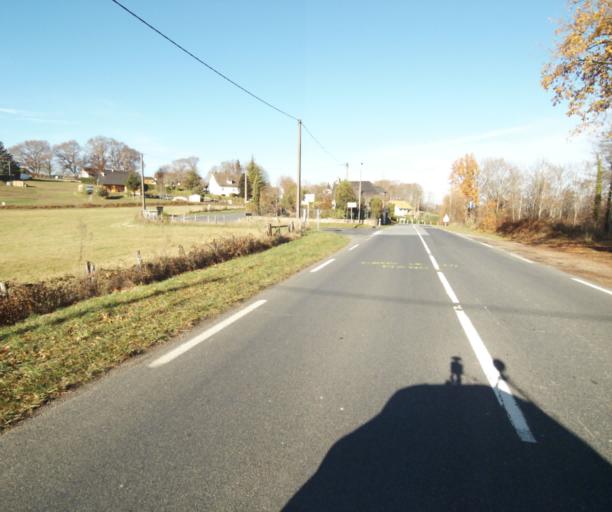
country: FR
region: Limousin
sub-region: Departement de la Correze
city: Sainte-Fortunade
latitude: 45.2252
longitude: 1.7662
